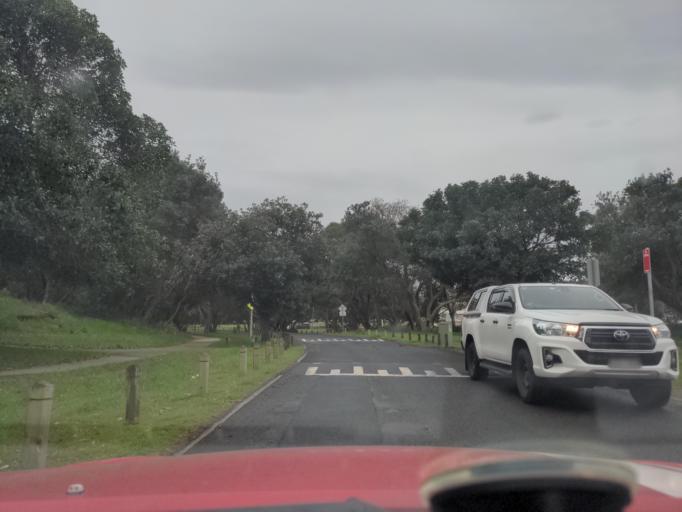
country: AU
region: New South Wales
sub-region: Randwick
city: Malabar
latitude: -33.9495
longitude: 151.2539
